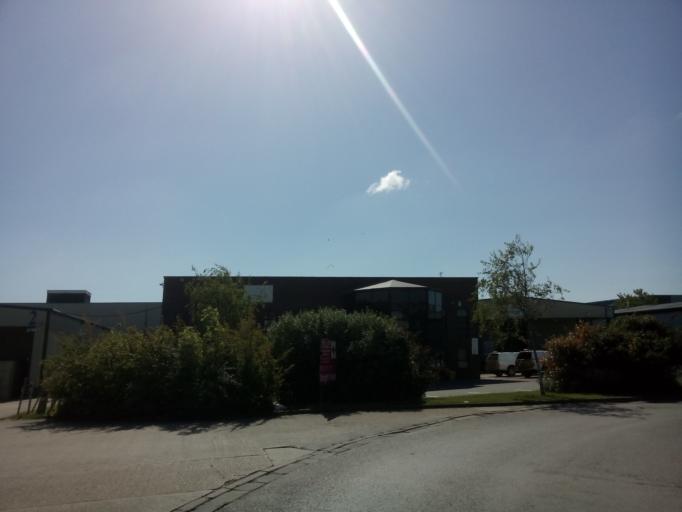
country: GB
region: England
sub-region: County Durham
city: West Rainton
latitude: 54.7928
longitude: -1.5342
